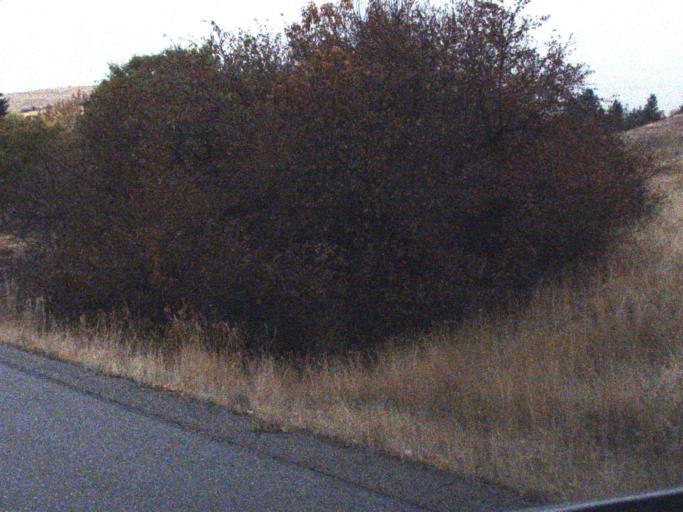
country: US
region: Washington
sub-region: Stevens County
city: Kettle Falls
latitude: 48.5964
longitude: -118.0042
